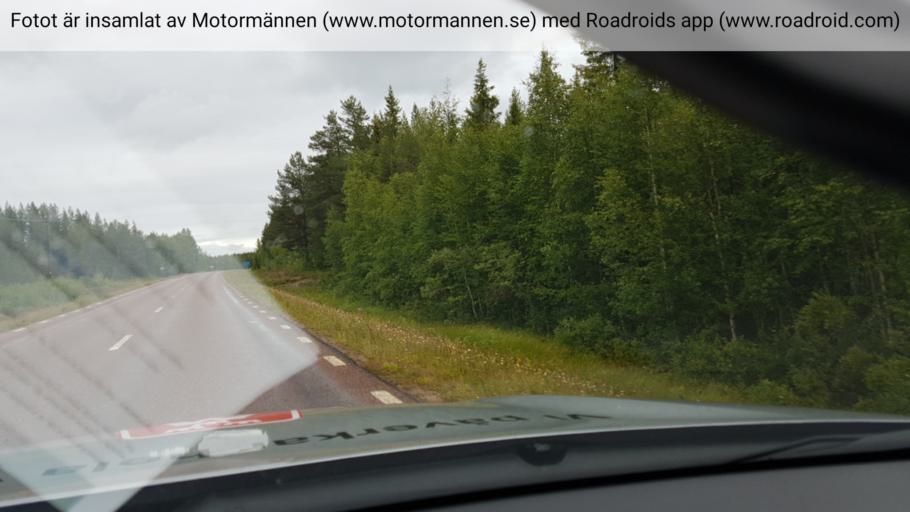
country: SE
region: Norrbotten
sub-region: Pajala Kommun
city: Pajala
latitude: 67.1341
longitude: 22.6090
